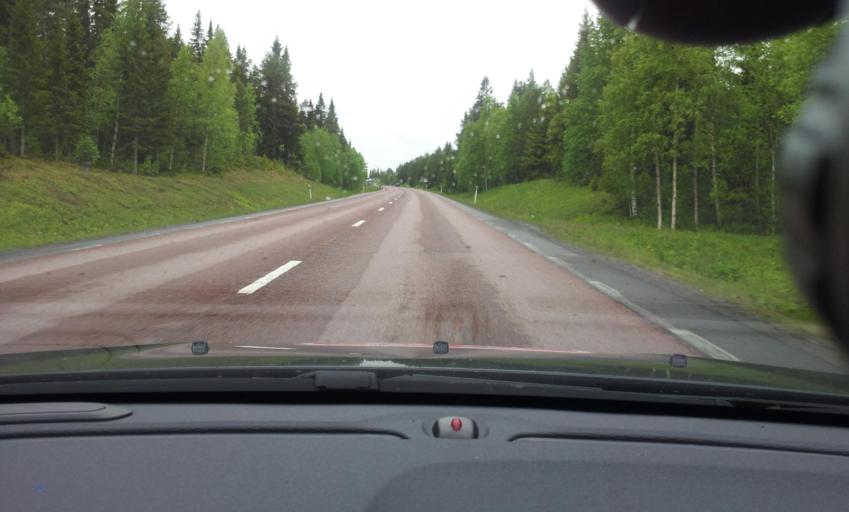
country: SE
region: Jaemtland
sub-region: Krokoms Kommun
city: Valla
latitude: 63.3269
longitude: 13.9585
